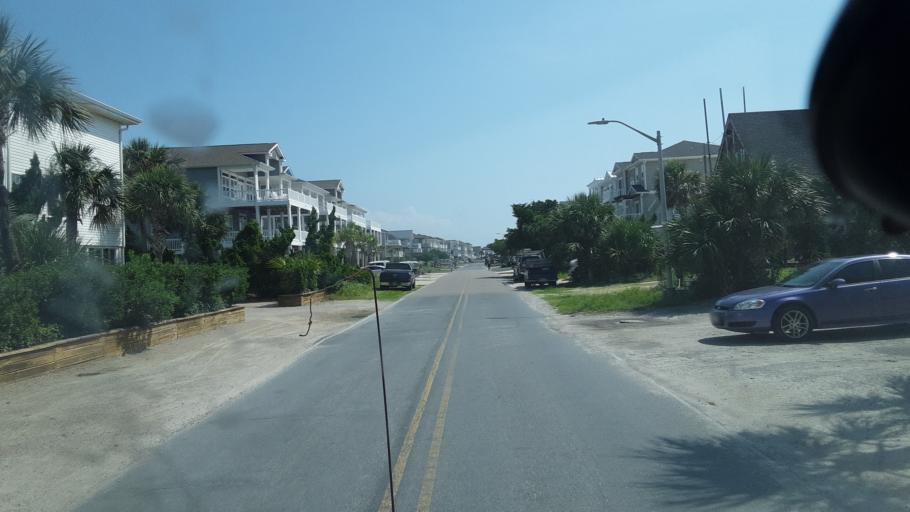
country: US
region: North Carolina
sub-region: Brunswick County
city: Shallotte
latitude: 33.8943
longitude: -78.4104
